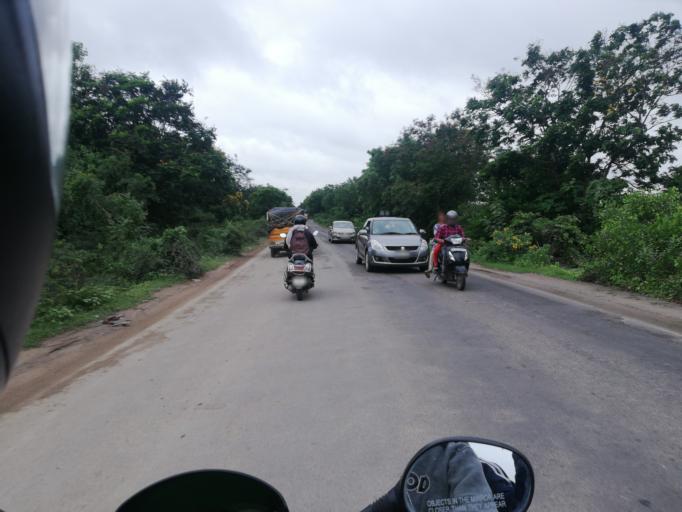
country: IN
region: Telangana
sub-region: Rangareddi
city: Quthbullapur
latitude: 17.5617
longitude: 78.4123
